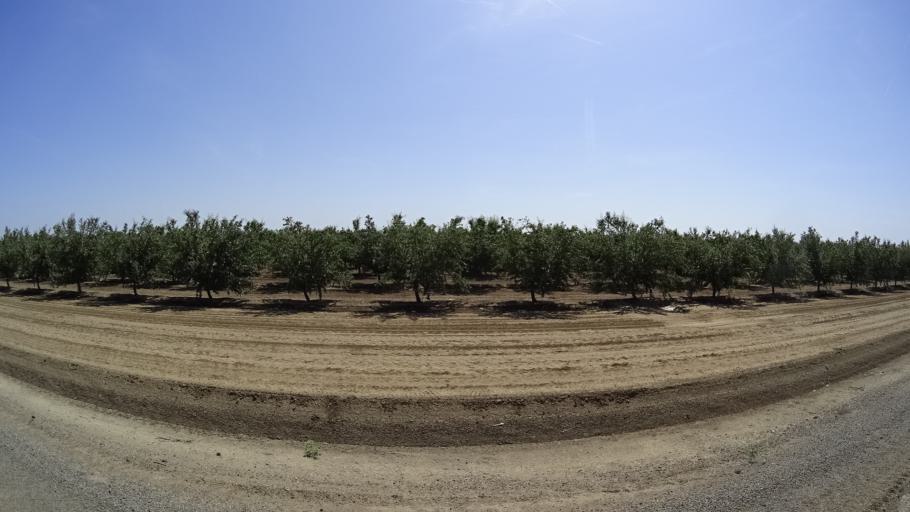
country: US
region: California
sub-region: Kings County
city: Kettleman City
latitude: 36.0893
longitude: -120.0037
